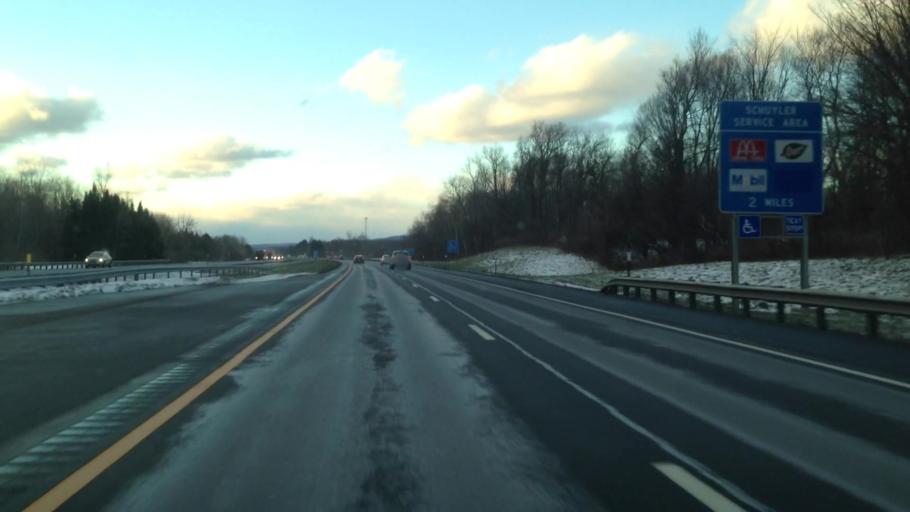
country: US
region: New York
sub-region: Herkimer County
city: Frankfort
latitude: 43.0564
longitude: -75.0685
